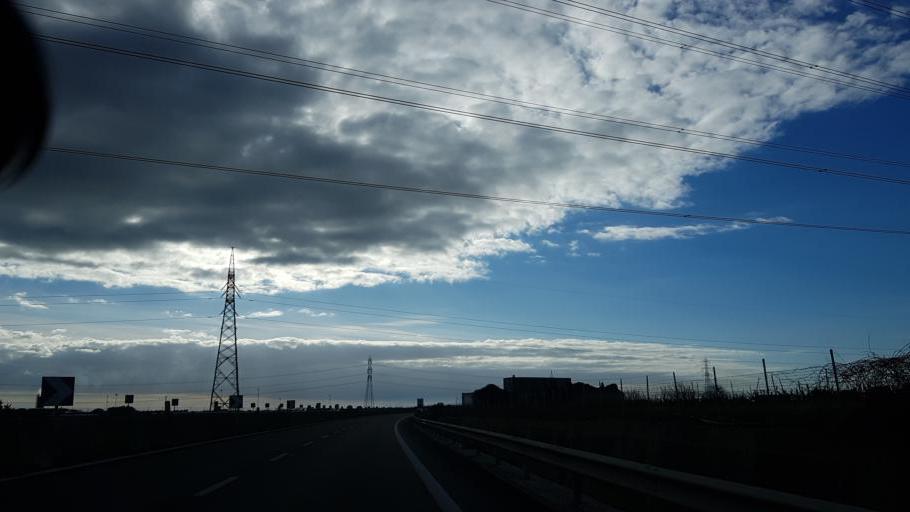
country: IT
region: Apulia
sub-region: Provincia di Brindisi
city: La Rosa
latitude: 40.6079
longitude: 17.9629
